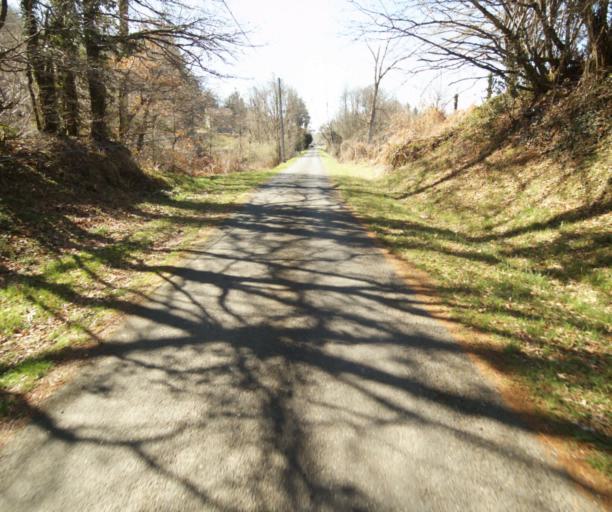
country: FR
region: Limousin
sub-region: Departement de la Correze
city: Saint-Clement
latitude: 45.3457
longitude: 1.6717
